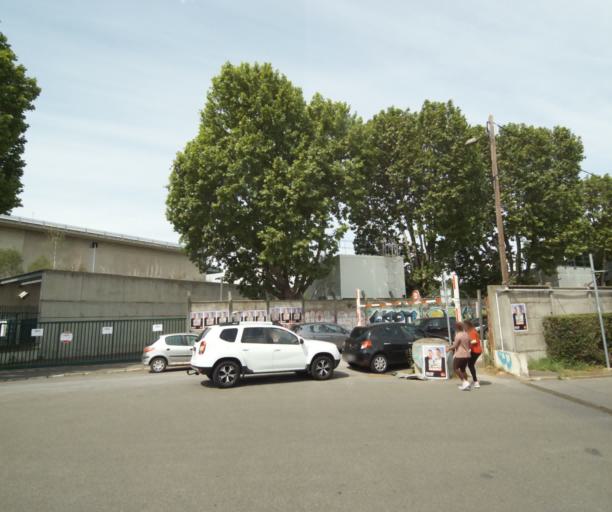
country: FR
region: Ile-de-France
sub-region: Departement du Val-d'Oise
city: Argenteuil
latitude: 48.9340
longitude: 2.2485
